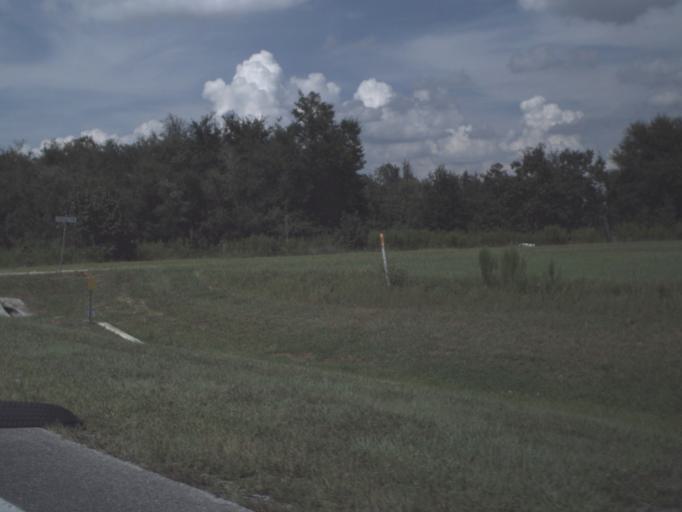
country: US
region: Florida
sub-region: Polk County
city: Crooked Lake Park
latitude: 27.8622
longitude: -81.5894
